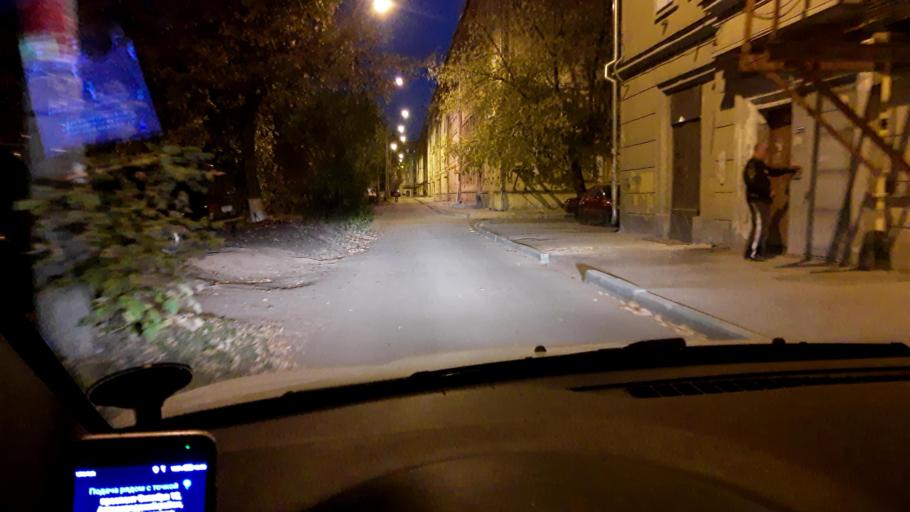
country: RU
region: Nizjnij Novgorod
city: Gorbatovka
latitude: 56.2515
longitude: 43.8627
